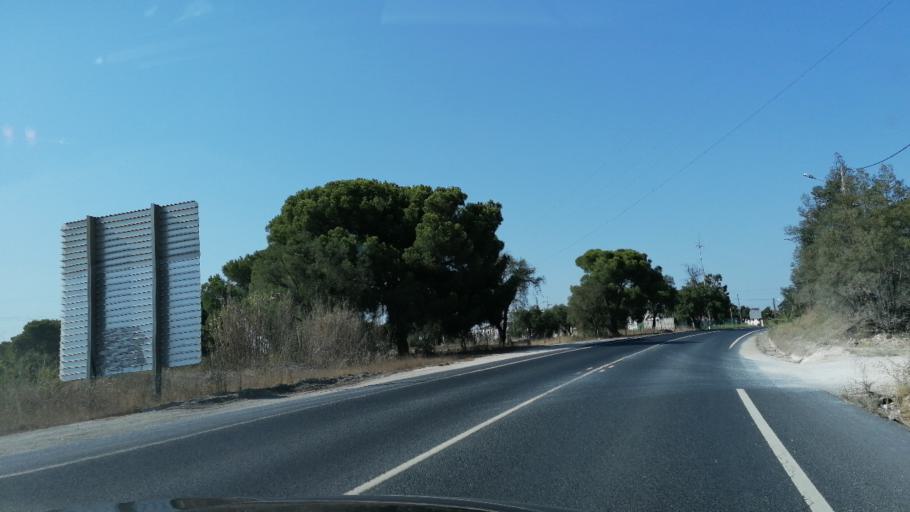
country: PT
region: Evora
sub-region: Vendas Novas
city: Vendas Novas
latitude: 38.6879
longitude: -8.6129
